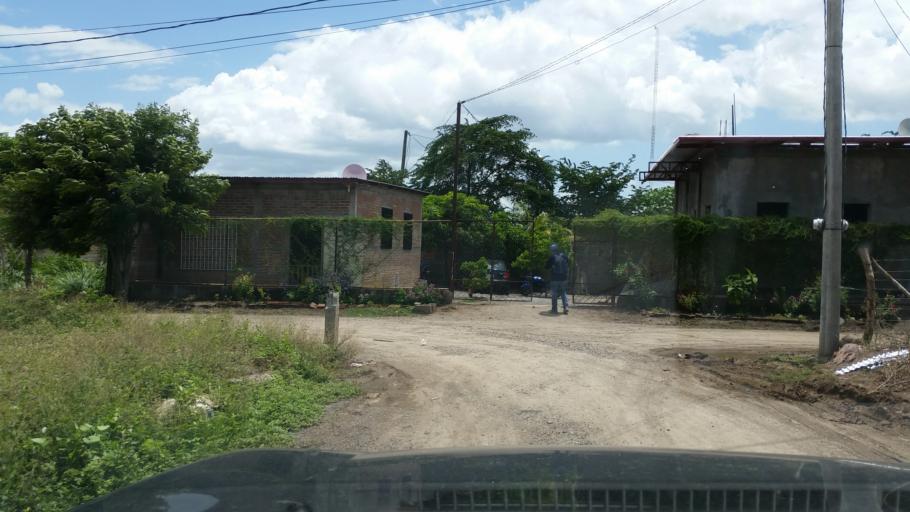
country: NI
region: Matagalpa
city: Ciudad Dario
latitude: 12.8648
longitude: -86.0910
